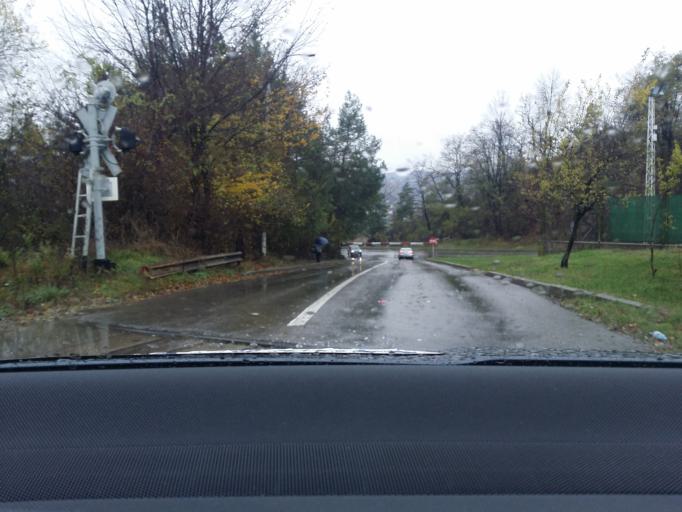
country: RO
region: Prahova
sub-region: Municipiul Campina
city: Campina
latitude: 45.1287
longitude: 25.7216
